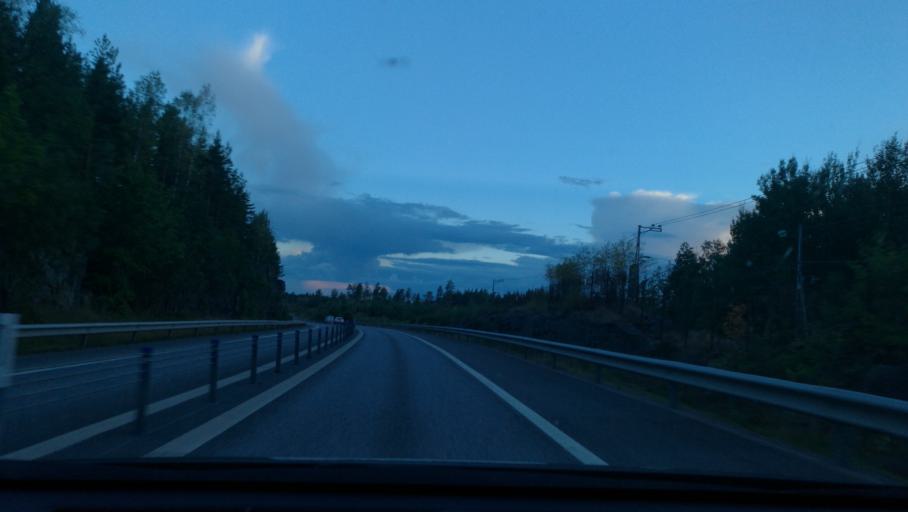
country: SE
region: OEstergoetland
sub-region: Norrkopings Kommun
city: Jursla
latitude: 58.8139
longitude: 16.1549
